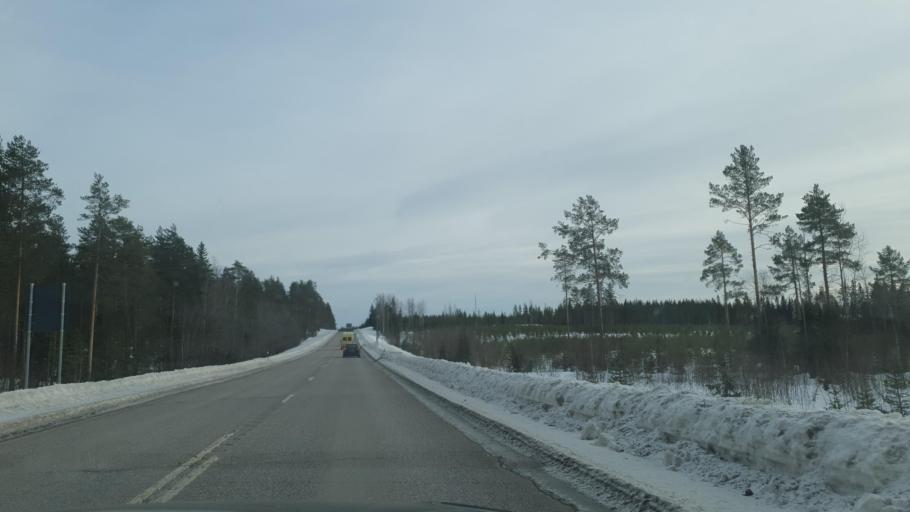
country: FI
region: Kainuu
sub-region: Kajaani
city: Kajaani
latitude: 64.4557
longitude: 27.4965
